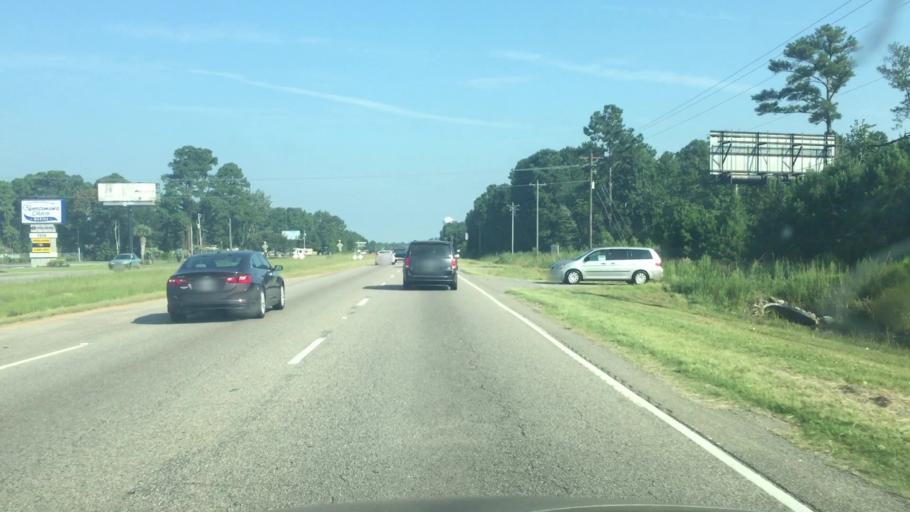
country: US
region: South Carolina
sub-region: Horry County
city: North Myrtle Beach
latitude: 33.8922
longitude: -78.6920
